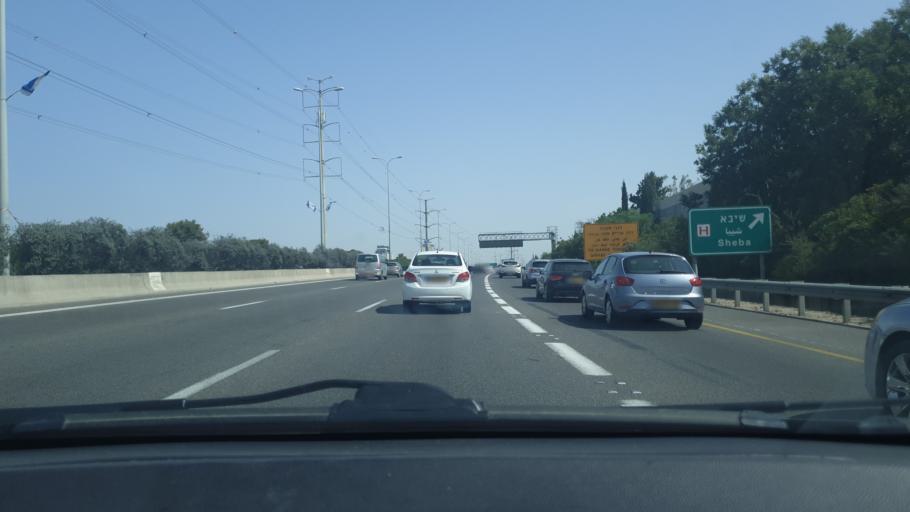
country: IL
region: Tel Aviv
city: Giv`atayim
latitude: 32.0472
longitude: 34.8303
